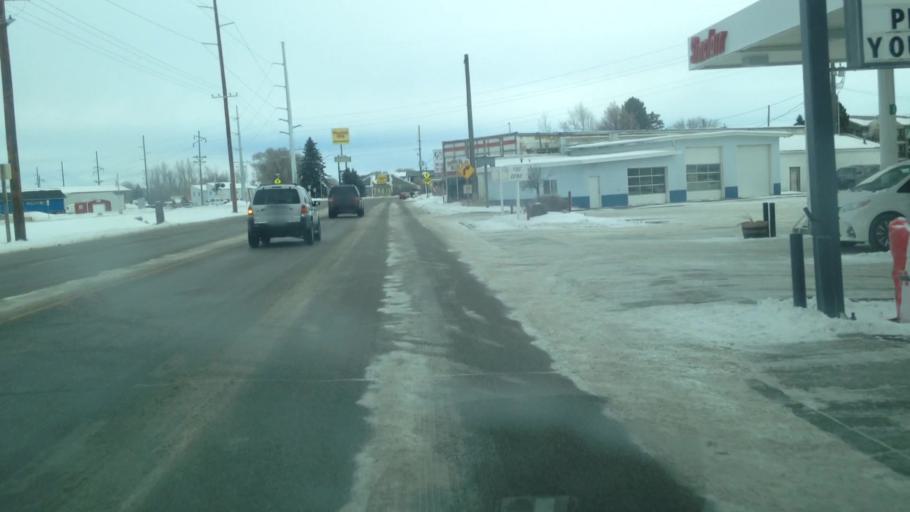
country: US
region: Idaho
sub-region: Madison County
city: Rexburg
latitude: 43.8157
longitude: -111.7992
